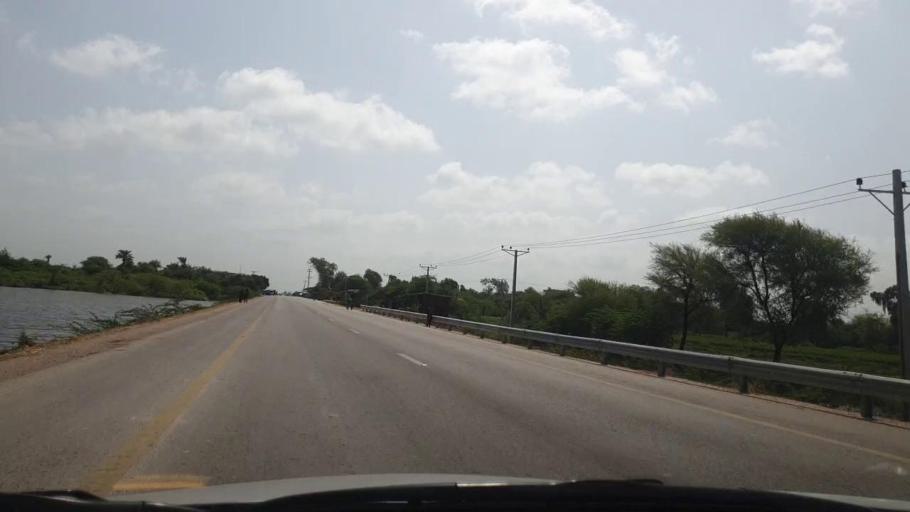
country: PK
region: Sindh
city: Talhar
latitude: 24.9092
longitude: 68.7350
